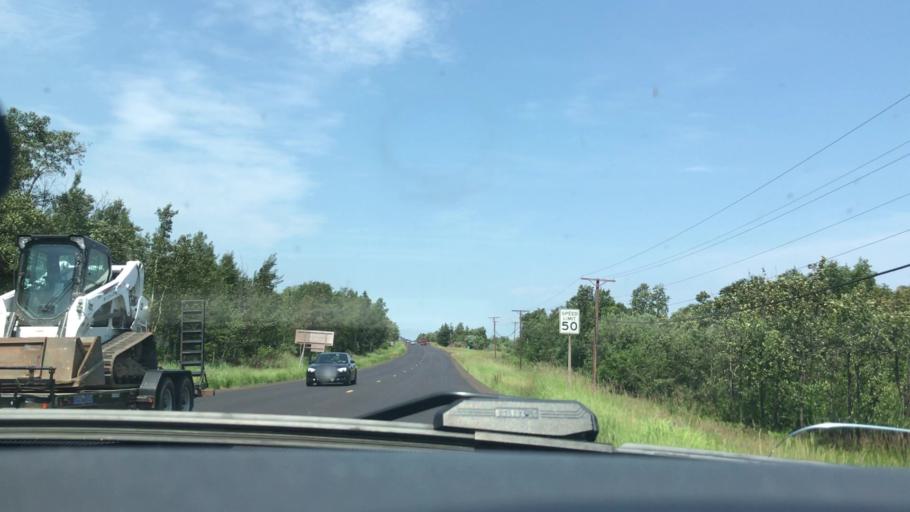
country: US
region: Minnesota
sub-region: Lake County
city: Silver Bay
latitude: 47.2777
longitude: -91.2730
